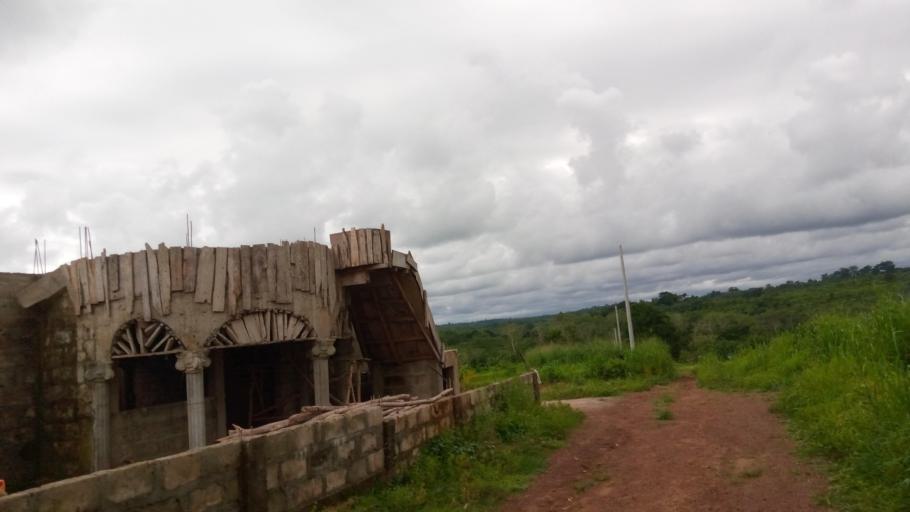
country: SL
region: Southern Province
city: Moyamba
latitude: 8.1654
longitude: -12.4471
